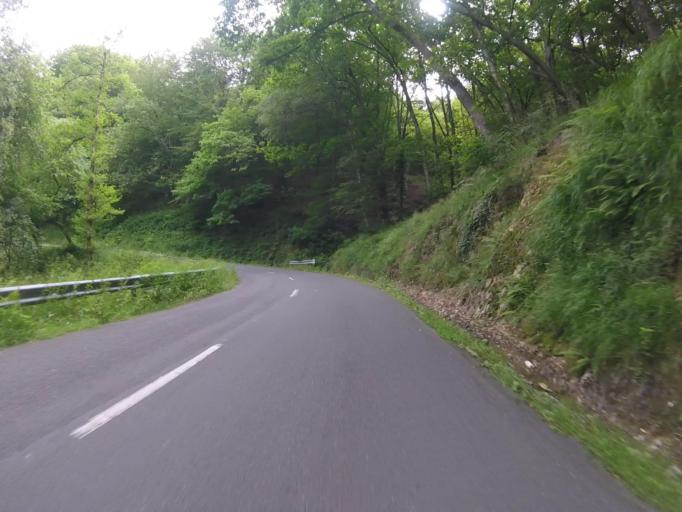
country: ES
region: Basque Country
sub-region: Provincia de Guipuzcoa
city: Errenteria
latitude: 43.2711
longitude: -1.8462
